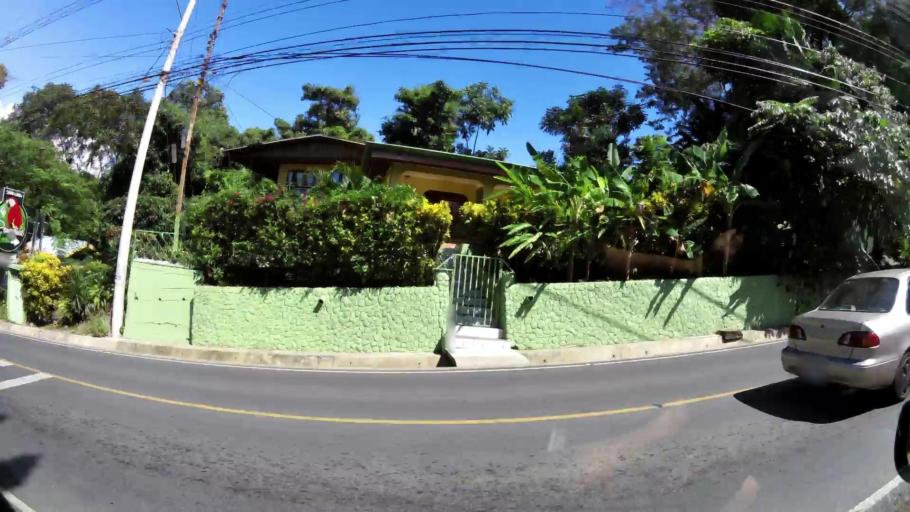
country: CR
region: Puntarenas
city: Quepos
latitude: 9.4114
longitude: -84.1550
